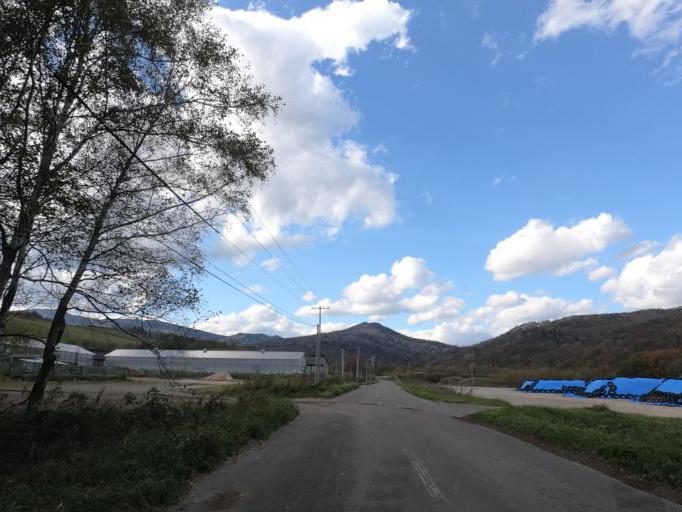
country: JP
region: Hokkaido
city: Otofuke
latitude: 43.2872
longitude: 143.2323
